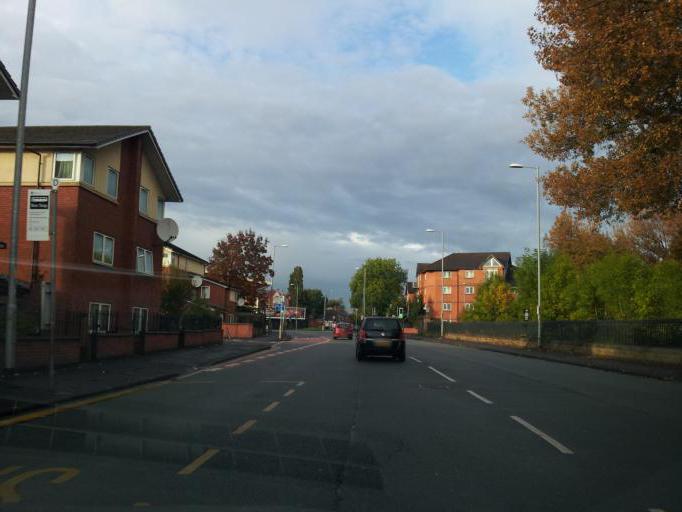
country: GB
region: England
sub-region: Manchester
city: Cheetham Hill
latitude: 53.5036
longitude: -2.2357
